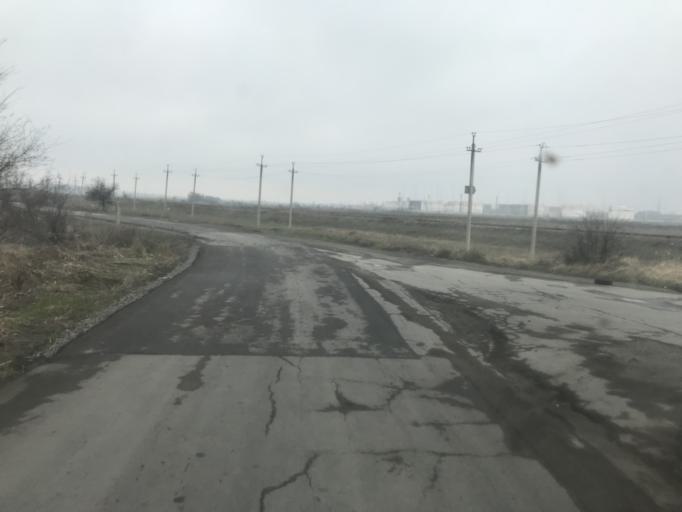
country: RU
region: Volgograd
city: Svetlyy Yar
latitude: 48.4927
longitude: 44.6573
